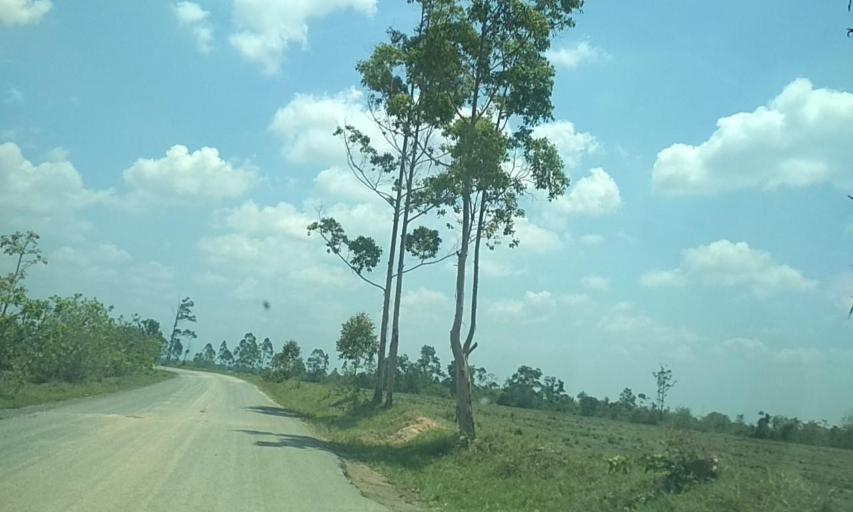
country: MX
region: Tabasco
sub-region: Huimanguillo
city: Francisco Rueda
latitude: 17.8093
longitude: -93.8678
